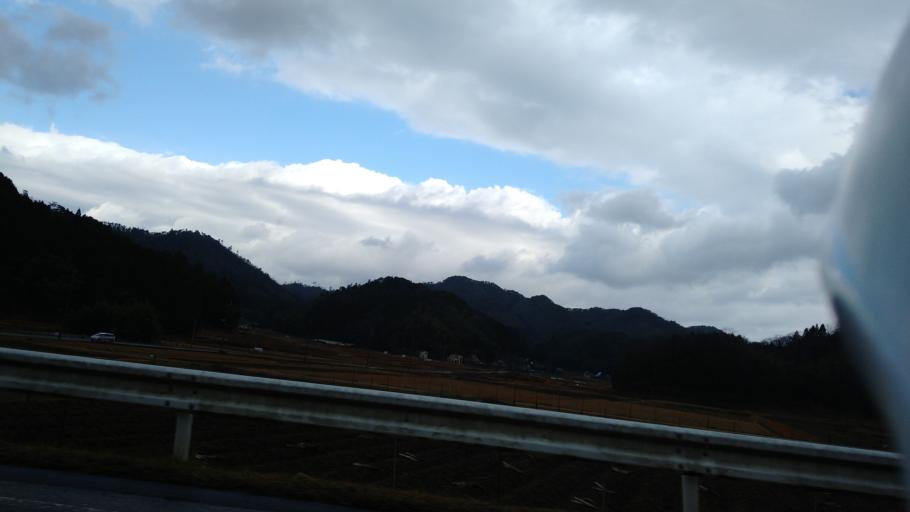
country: JP
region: Hyogo
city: Sasayama
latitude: 35.0748
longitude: 135.3764
